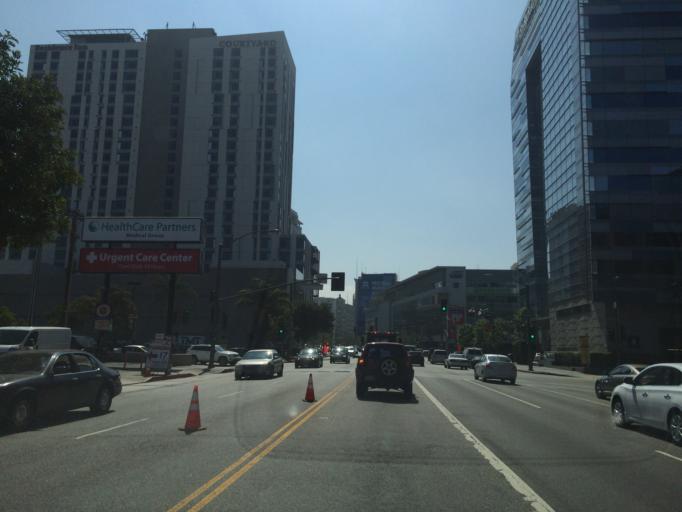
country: US
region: California
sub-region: Los Angeles County
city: Los Angeles
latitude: 34.0461
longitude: -118.2674
